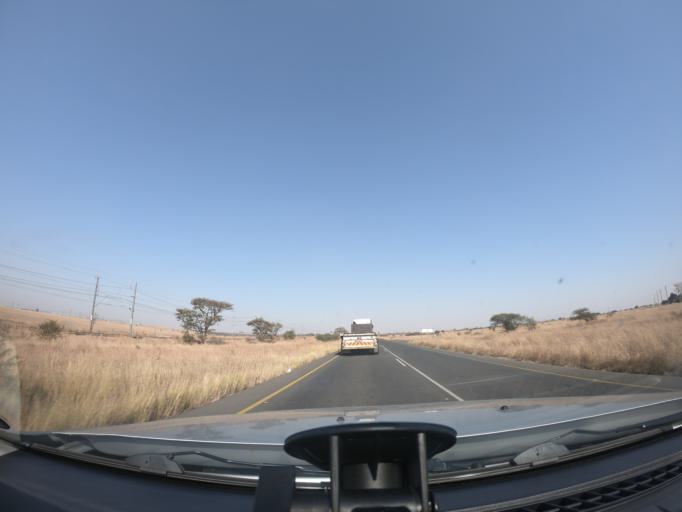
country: ZA
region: KwaZulu-Natal
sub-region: uThukela District Municipality
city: Ladysmith
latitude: -28.7577
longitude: 29.8212
